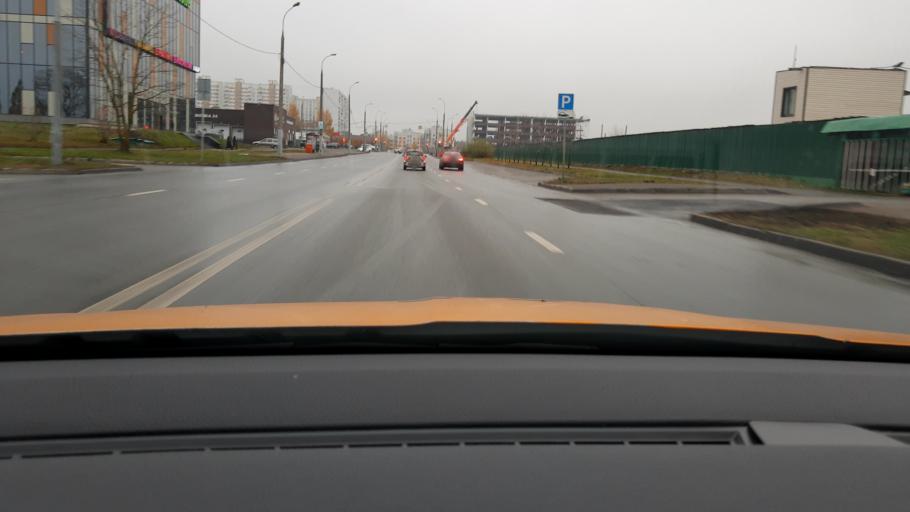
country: RU
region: Moscow
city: Novo-Peredelkino
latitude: 55.6383
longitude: 37.3360
